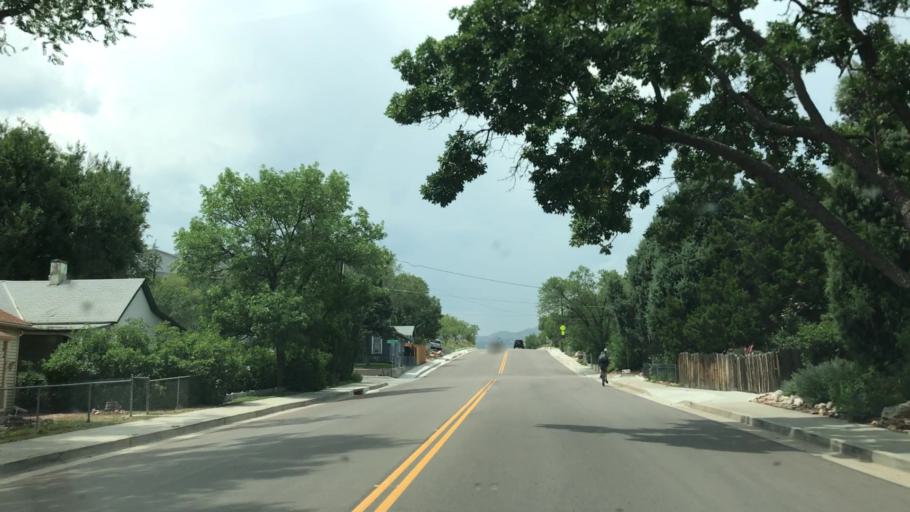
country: US
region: Colorado
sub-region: El Paso County
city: Colorado Springs
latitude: 38.8503
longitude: -104.8587
